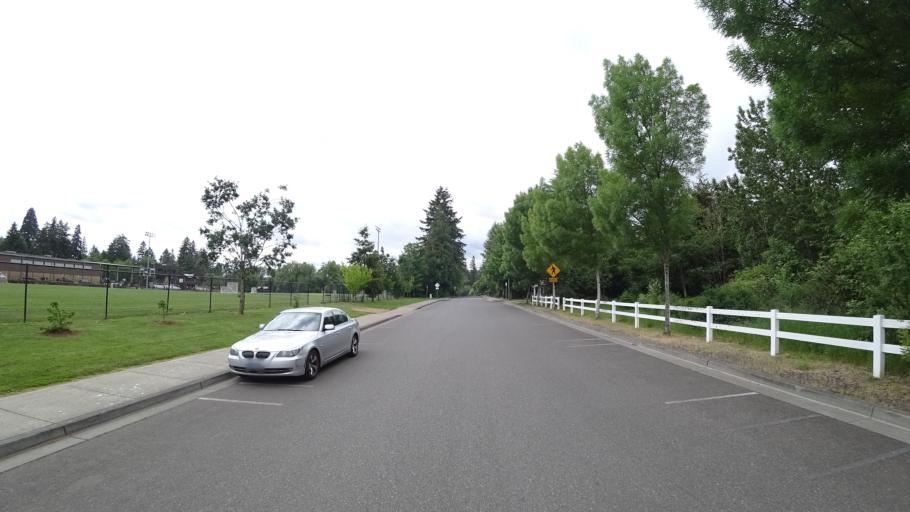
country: US
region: Oregon
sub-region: Washington County
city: Raleigh Hills
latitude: 45.4767
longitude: -122.7546
